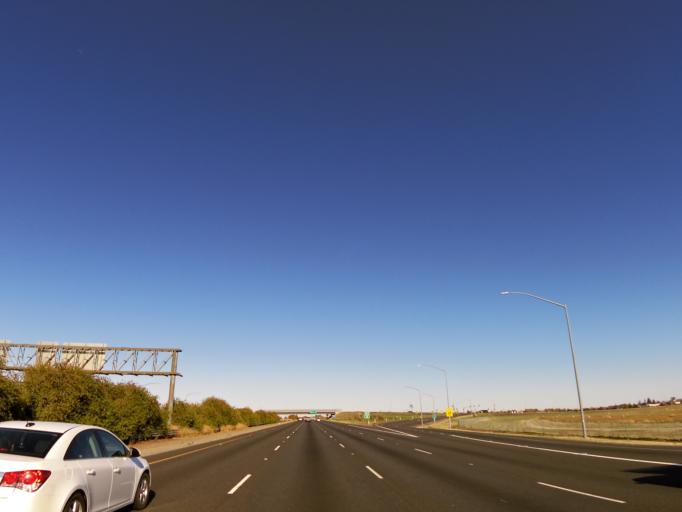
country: US
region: California
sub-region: Yolo County
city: West Sacramento
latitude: 38.6383
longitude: -121.5234
